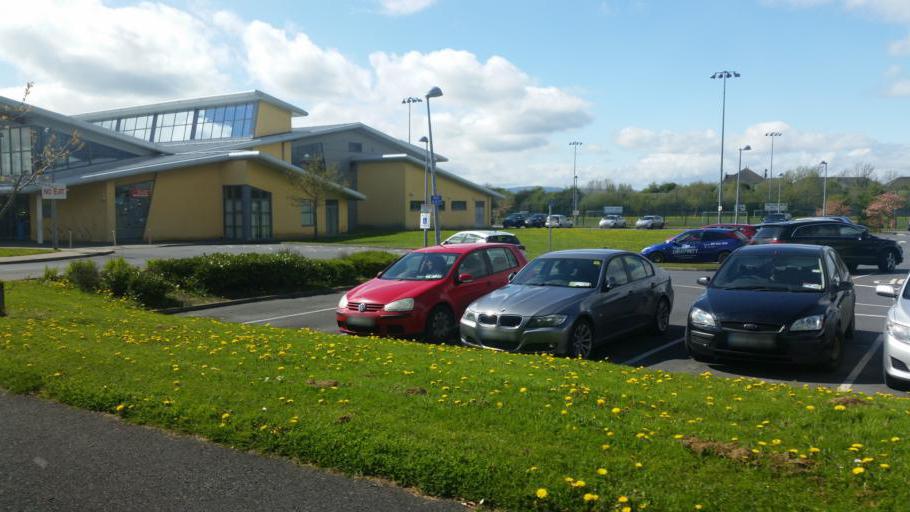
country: IE
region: Leinster
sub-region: Laois
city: Portlaoise
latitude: 53.0382
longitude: -7.2948
